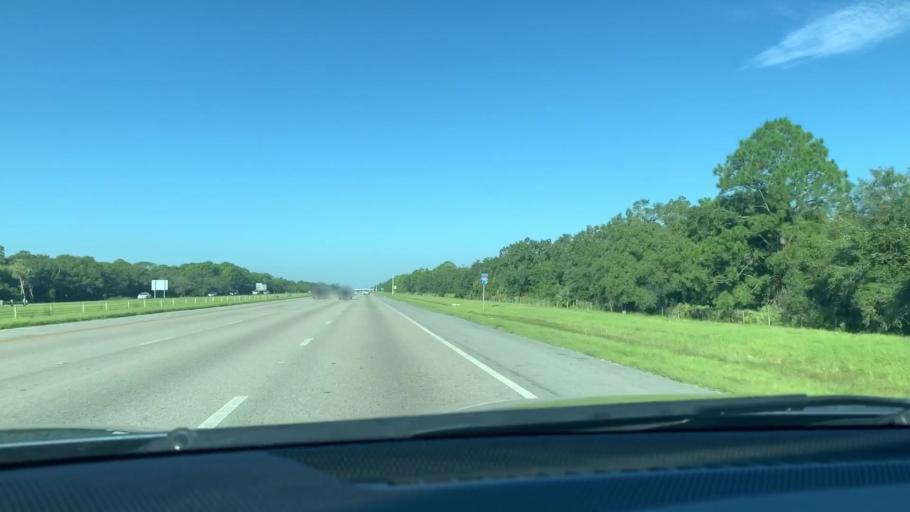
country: US
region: Florida
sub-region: Sarasota County
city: North Port
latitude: 27.1000
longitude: -82.2111
